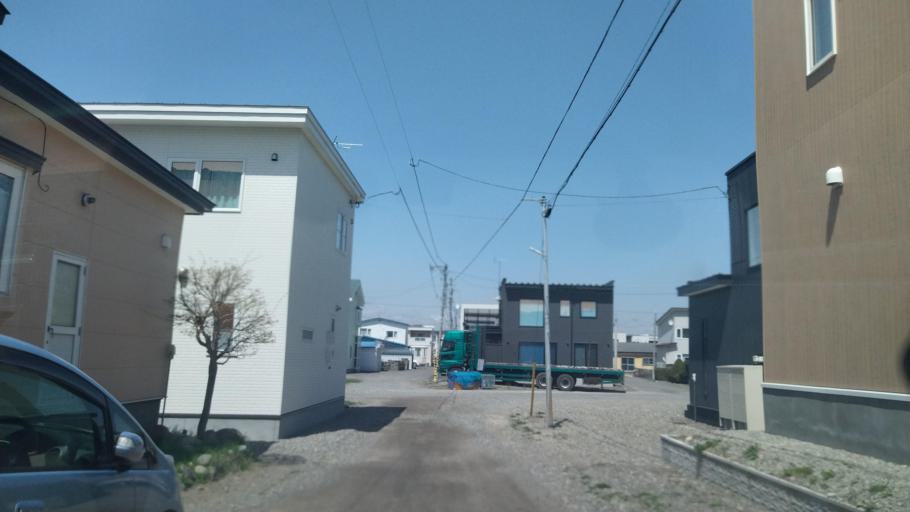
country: JP
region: Hokkaido
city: Obihiro
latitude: 42.9312
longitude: 143.1741
